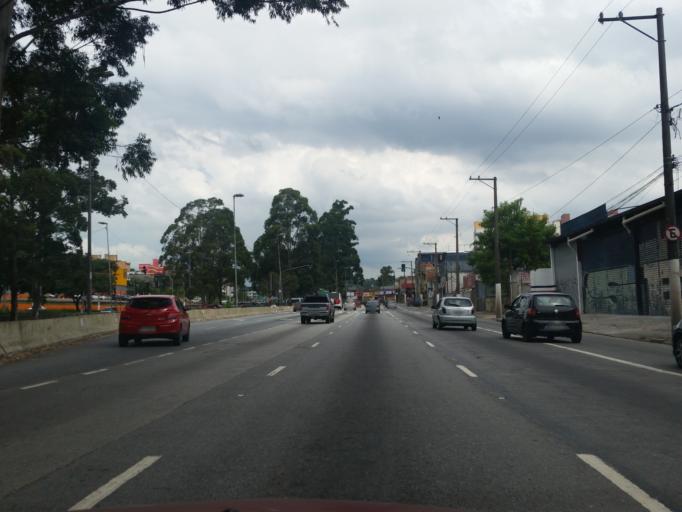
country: BR
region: Sao Paulo
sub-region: Ferraz De Vasconcelos
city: Ferraz de Vasconcelos
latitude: -23.5508
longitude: -46.4465
